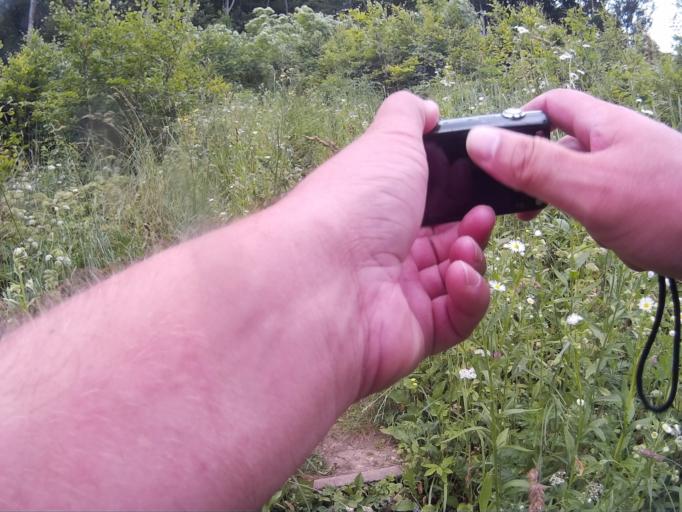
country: HU
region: Veszprem
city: Herend
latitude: 47.1121
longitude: 17.7836
